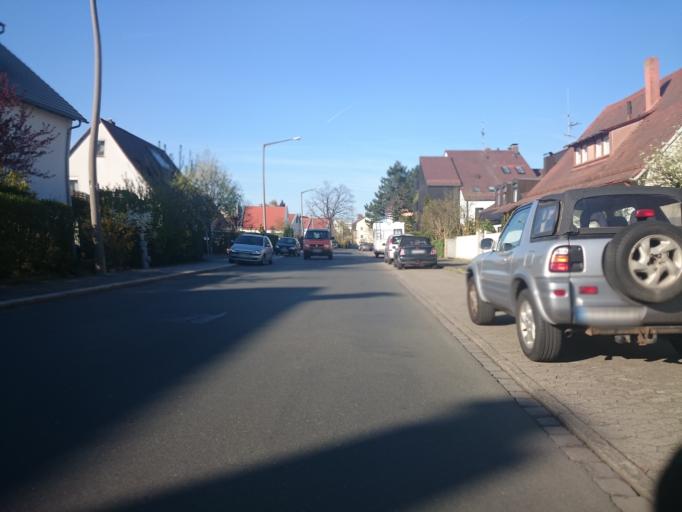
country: DE
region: Bavaria
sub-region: Regierungsbezirk Mittelfranken
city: Nuernberg
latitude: 49.4541
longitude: 11.1234
